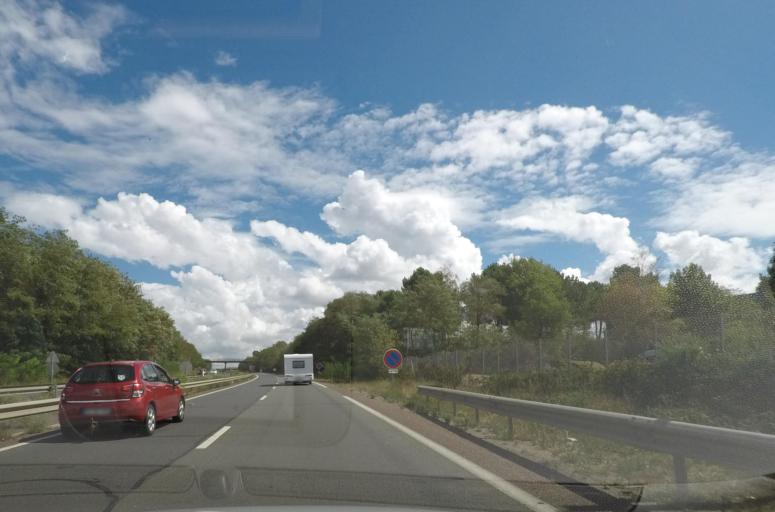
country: FR
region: Pays de la Loire
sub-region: Departement de la Sarthe
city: Arnage
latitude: 47.9577
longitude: 0.2087
